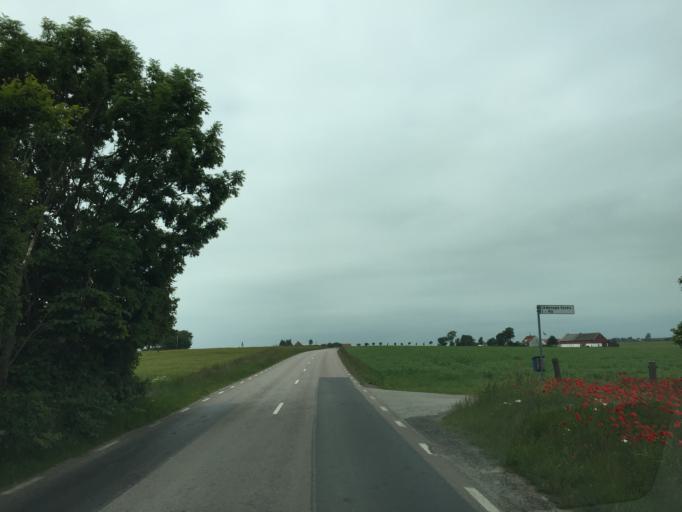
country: SE
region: Skane
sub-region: Ystads Kommun
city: Kopingebro
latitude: 55.4283
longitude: 14.0938
